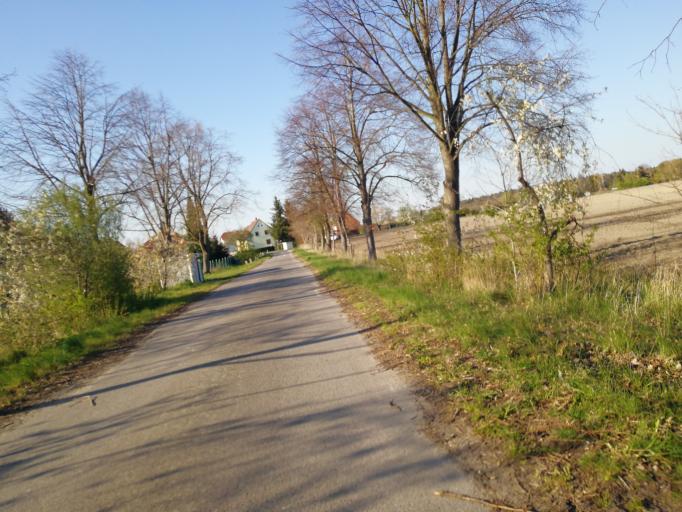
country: DE
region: Brandenburg
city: Calau
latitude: 51.7257
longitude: 13.9702
